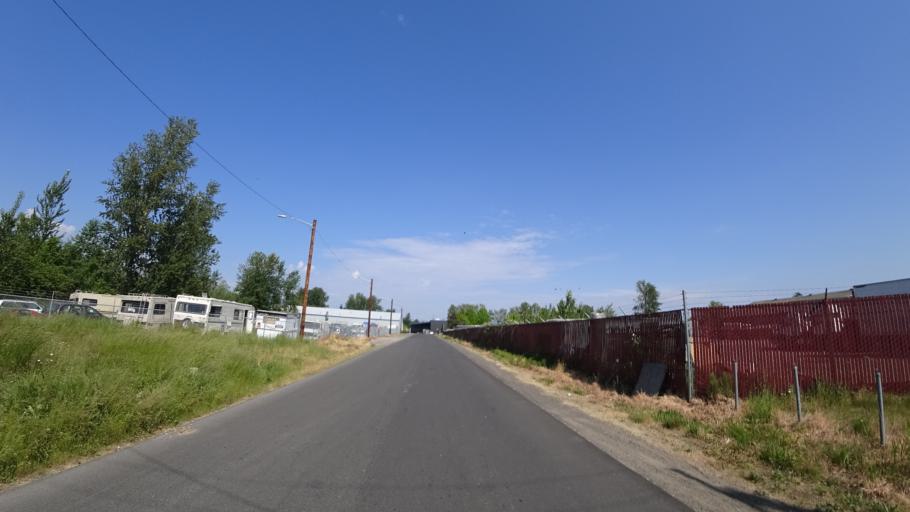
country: US
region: Oregon
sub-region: Multnomah County
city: Fairview
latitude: 45.5566
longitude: -122.5128
